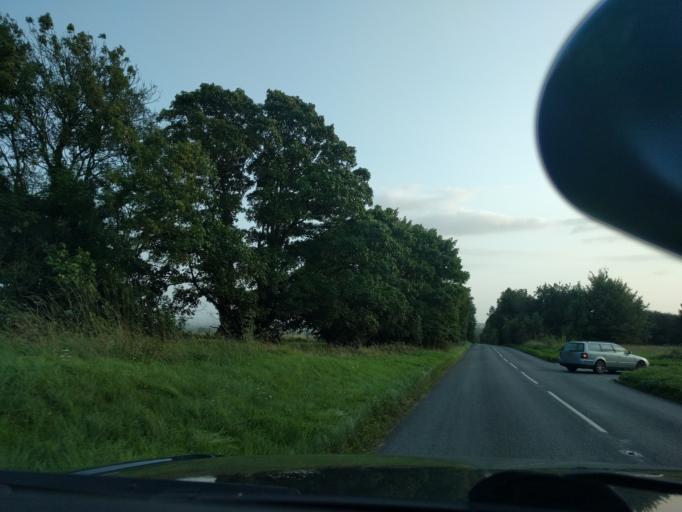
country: GB
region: England
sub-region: Wiltshire
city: Box
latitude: 51.4089
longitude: -2.2320
